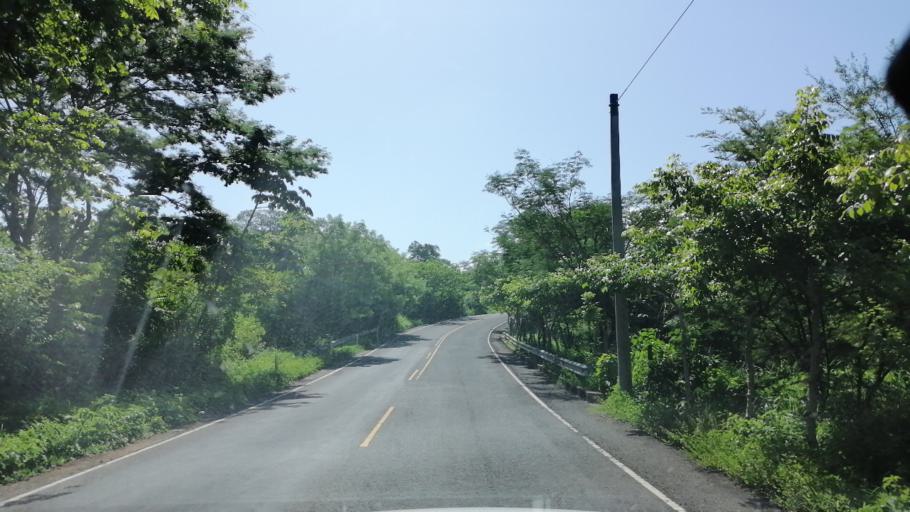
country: HN
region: Lempira
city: La Virtud
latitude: 13.9582
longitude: -88.7574
